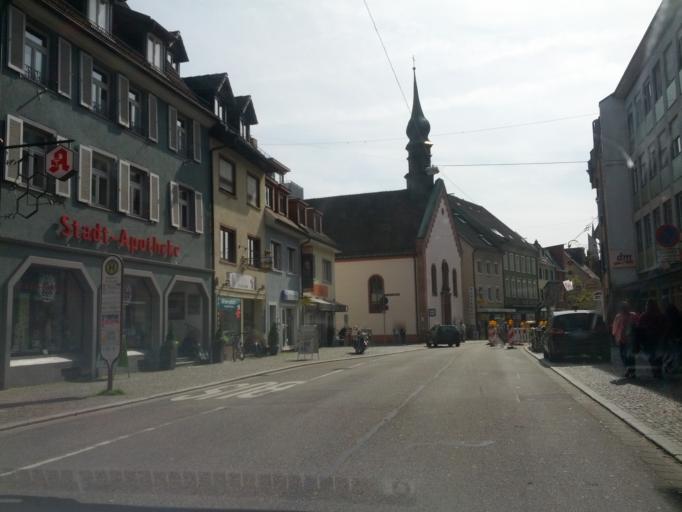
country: DE
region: Baden-Wuerttemberg
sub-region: Freiburg Region
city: Waldkirch
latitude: 48.0939
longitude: 7.9608
